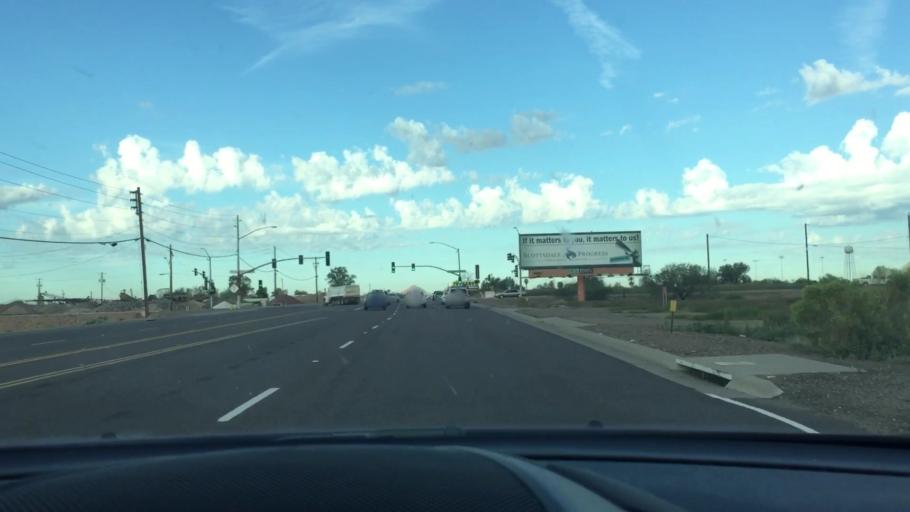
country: US
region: Arizona
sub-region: Maricopa County
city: Mesa
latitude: 33.4647
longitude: -111.8545
